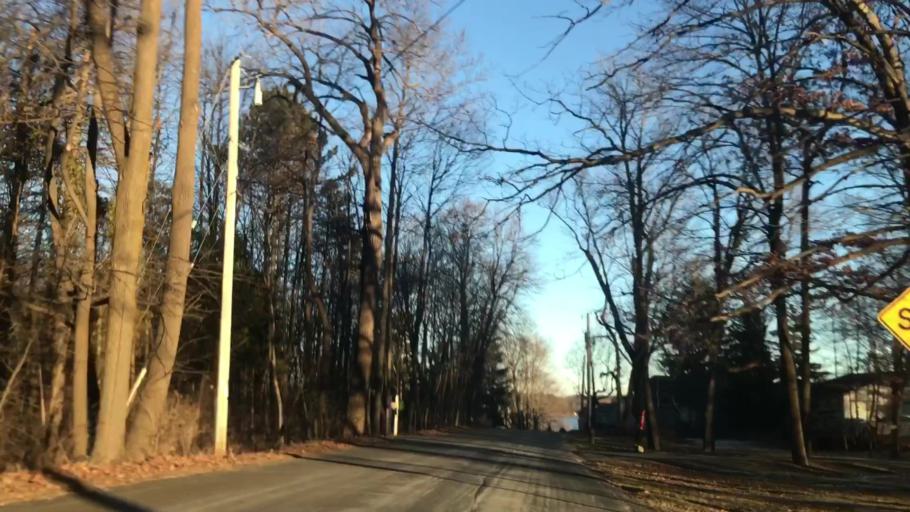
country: US
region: Wisconsin
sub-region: Washington County
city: Slinger
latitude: 43.3767
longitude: -88.2745
